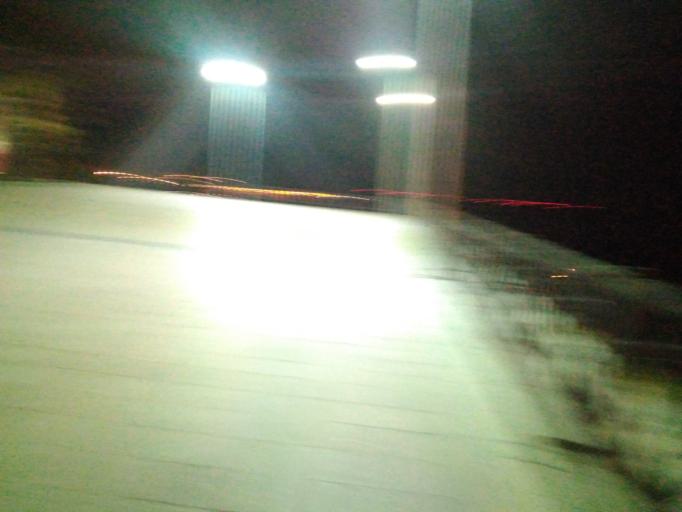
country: RU
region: Ulyanovsk
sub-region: Ulyanovskiy Rayon
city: Ulyanovsk
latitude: 54.3071
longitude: 48.3965
